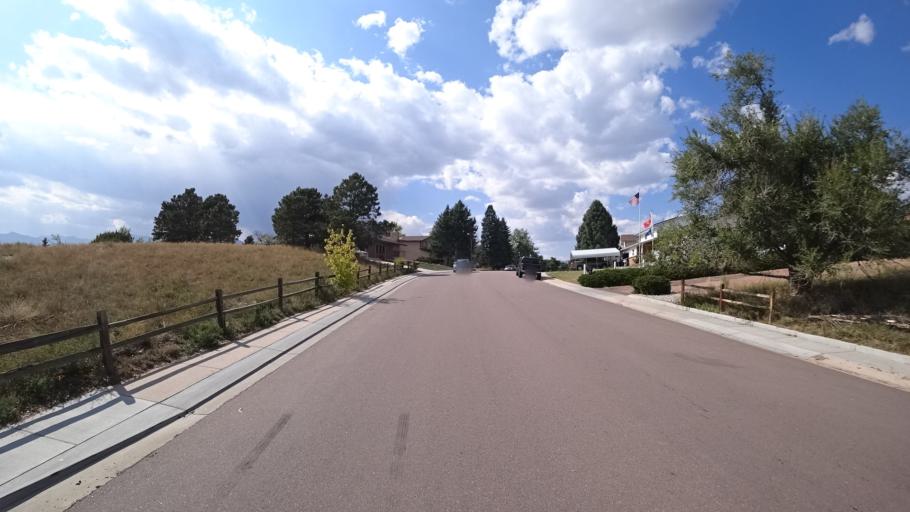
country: US
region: Colorado
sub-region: El Paso County
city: Cimarron Hills
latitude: 38.8729
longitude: -104.7310
